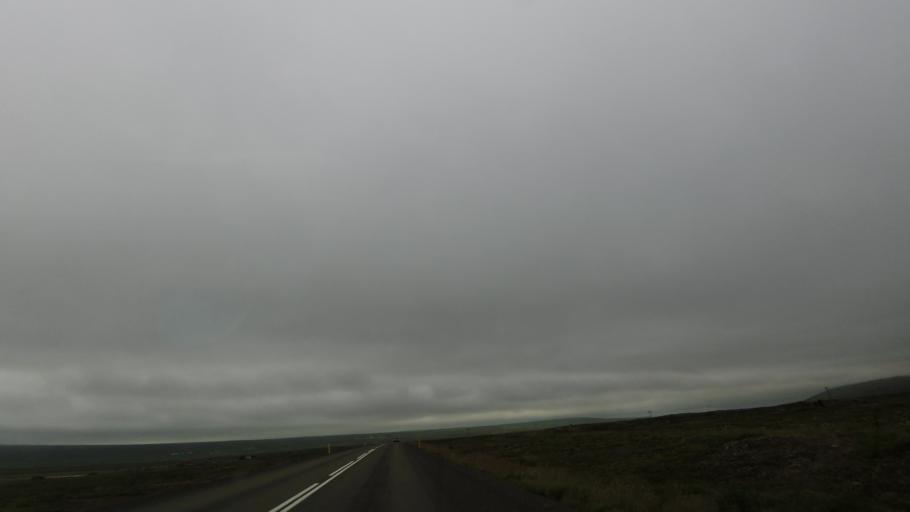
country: IS
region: Northeast
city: Laugar
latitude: 65.7008
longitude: -17.6003
